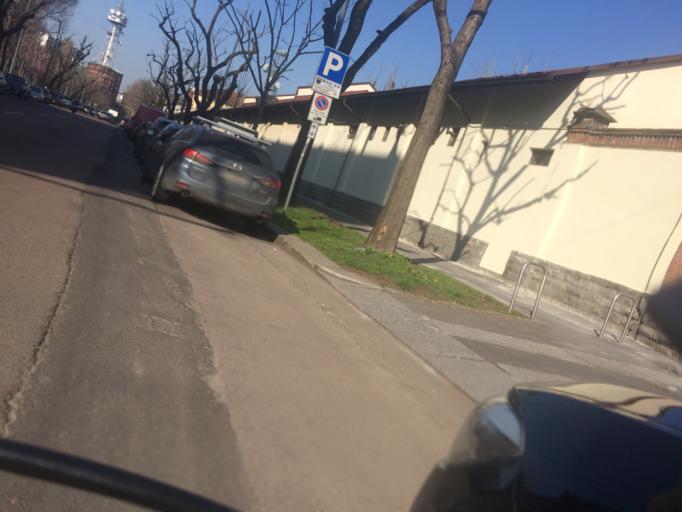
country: IT
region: Lombardy
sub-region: Citta metropolitana di Milano
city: Milano
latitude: 45.4725
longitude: 9.1635
